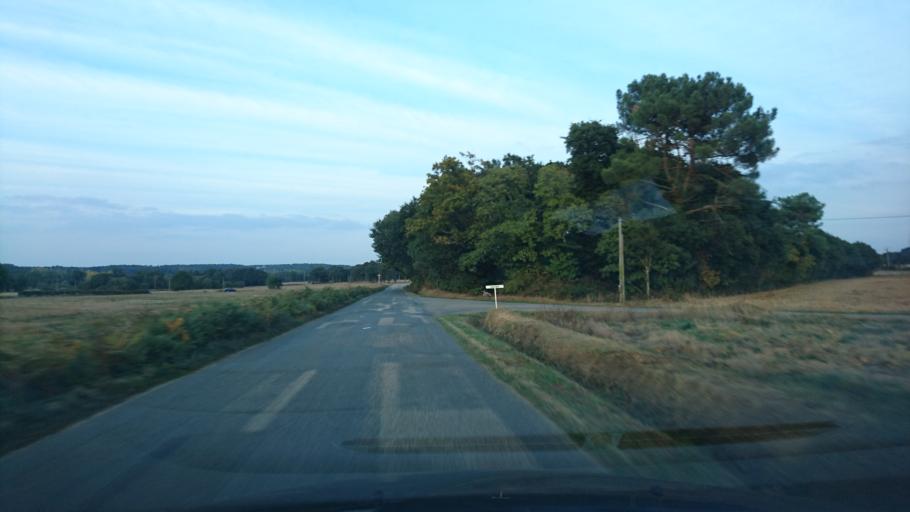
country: FR
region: Brittany
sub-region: Departement du Morbihan
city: Guer
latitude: 47.8867
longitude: -2.0609
